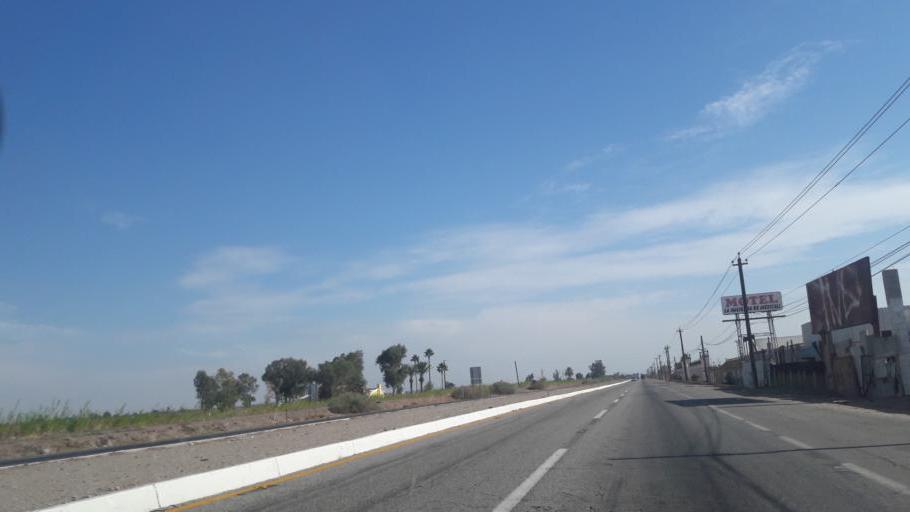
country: MX
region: Baja California
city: Progreso
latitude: 32.5894
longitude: -115.6112
